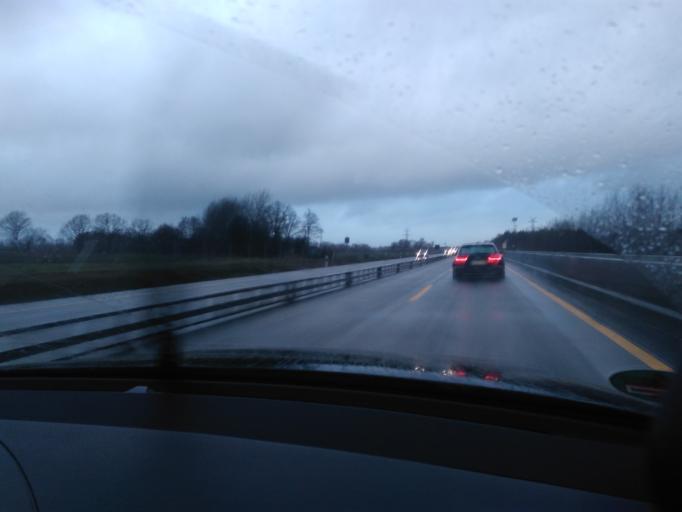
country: DE
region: Schleswig-Holstein
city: Bimohlen
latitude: 53.9468
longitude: 9.9489
